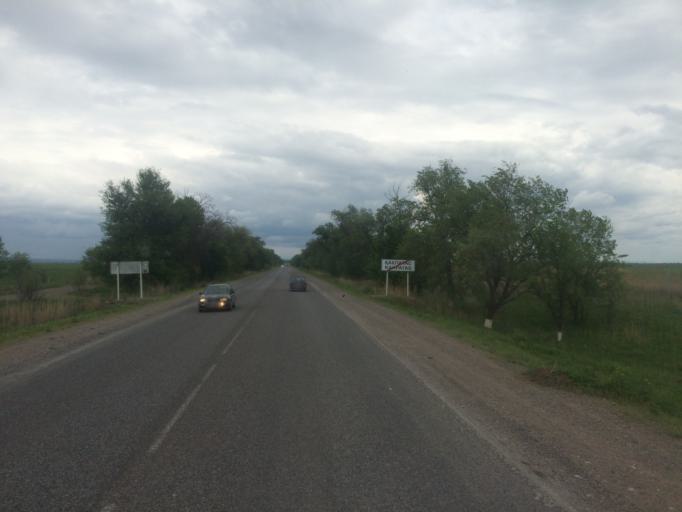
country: KZ
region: Zhambyl
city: Georgiyevka
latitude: 43.2261
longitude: 74.4067
